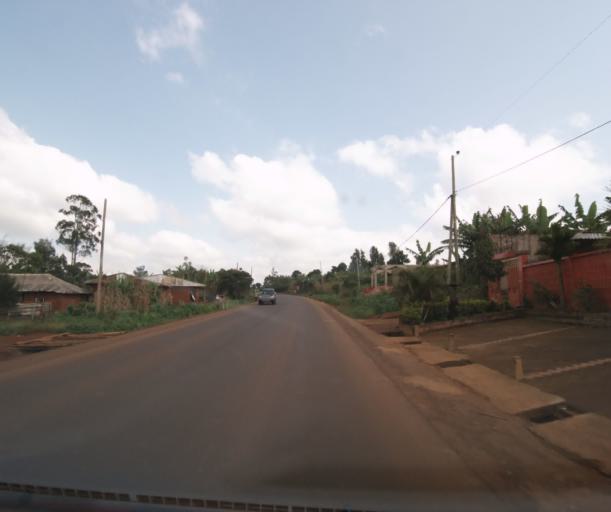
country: CM
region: West
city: Dschang
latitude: 5.4943
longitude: 10.1622
